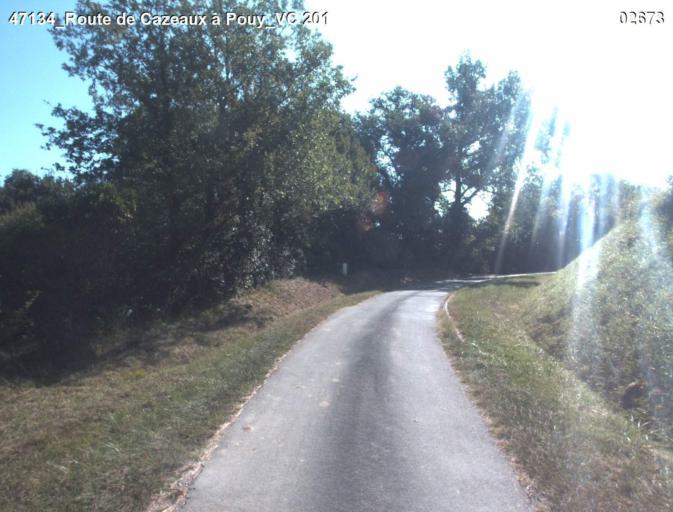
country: FR
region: Aquitaine
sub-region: Departement du Lot-et-Garonne
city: Mezin
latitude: 44.0243
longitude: 0.3117
